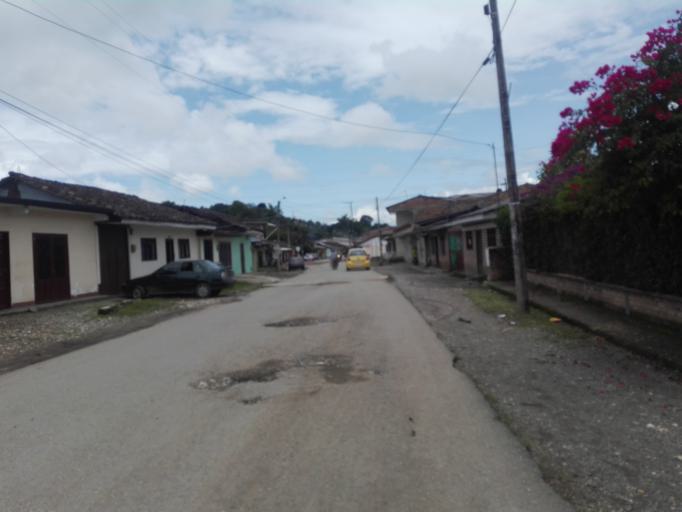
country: CO
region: Cauca
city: Popayan
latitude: 2.3511
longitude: -76.6748
